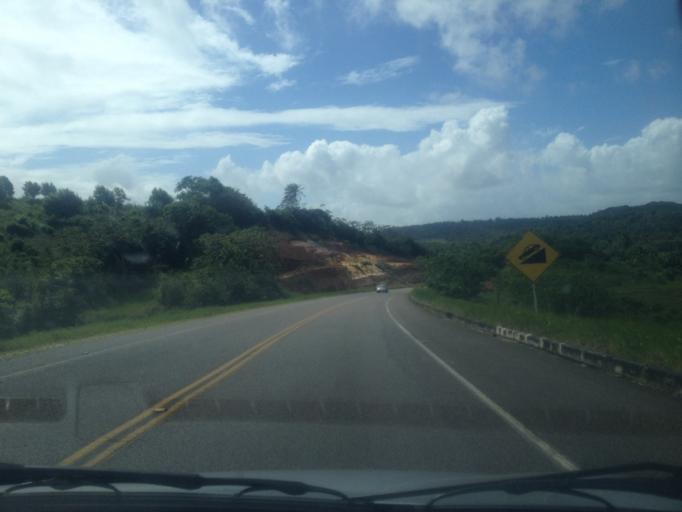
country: BR
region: Bahia
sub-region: Conde
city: Conde
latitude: -11.7774
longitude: -37.6117
